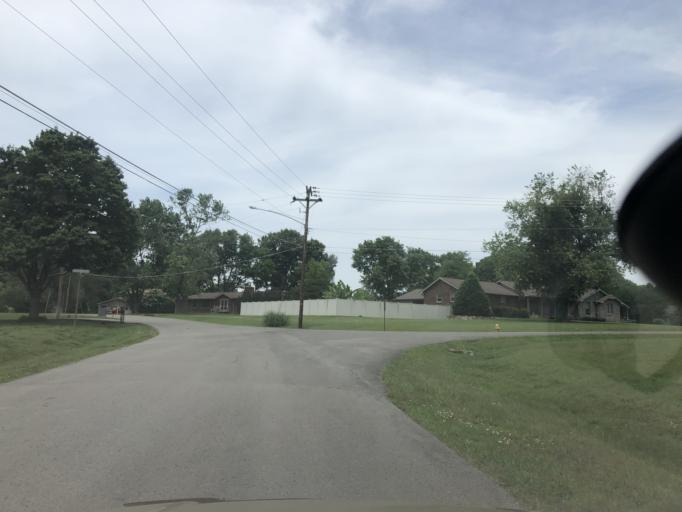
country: US
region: Tennessee
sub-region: Davidson County
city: Lakewood
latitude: 36.2587
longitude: -86.5952
